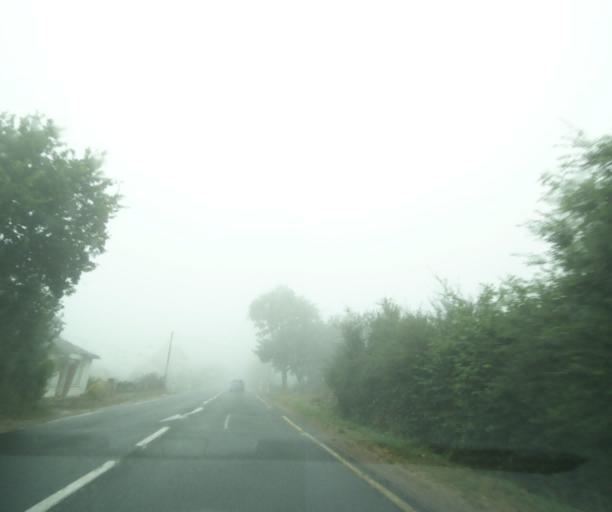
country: FR
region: Midi-Pyrenees
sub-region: Departement de l'Aveyron
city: Baraqueville
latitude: 44.2293
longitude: 2.4120
